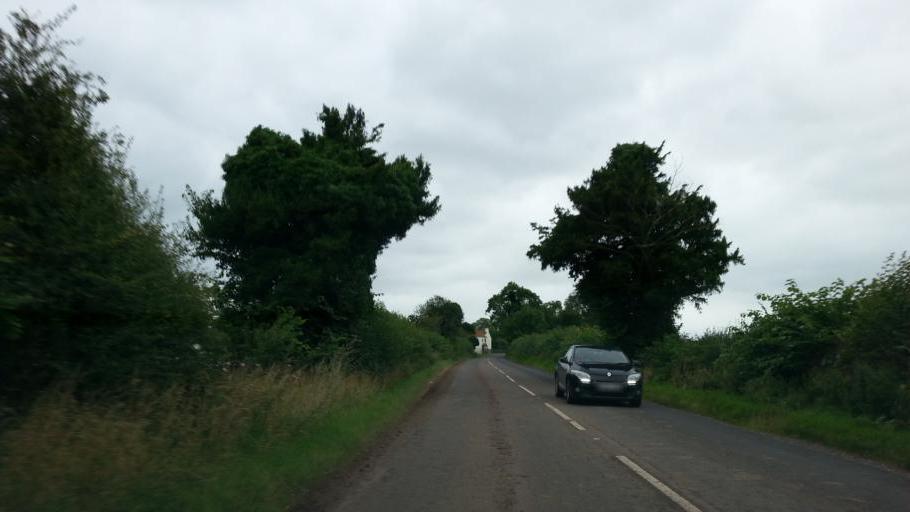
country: GB
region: England
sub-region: Nottinghamshire
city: Farnsfield
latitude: 53.0719
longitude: -1.0012
